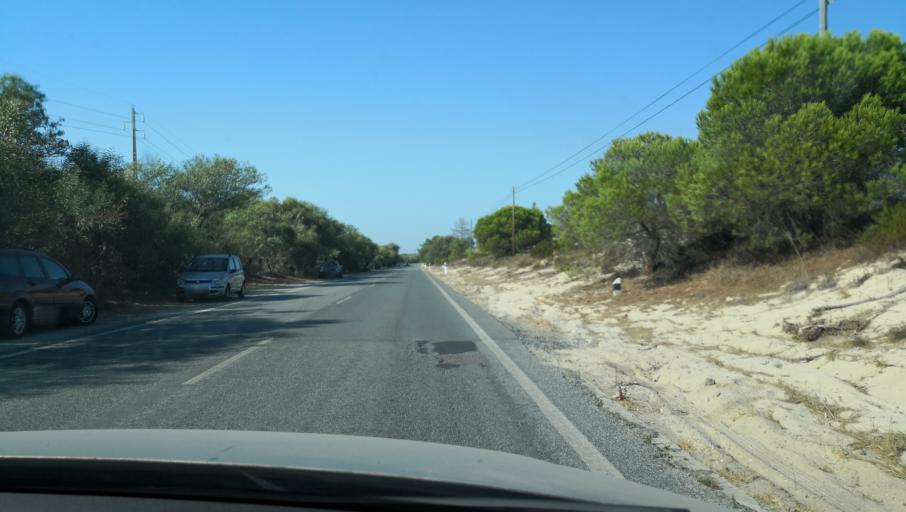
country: PT
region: Setubal
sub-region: Setubal
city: Setubal
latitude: 38.3939
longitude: -8.8036
